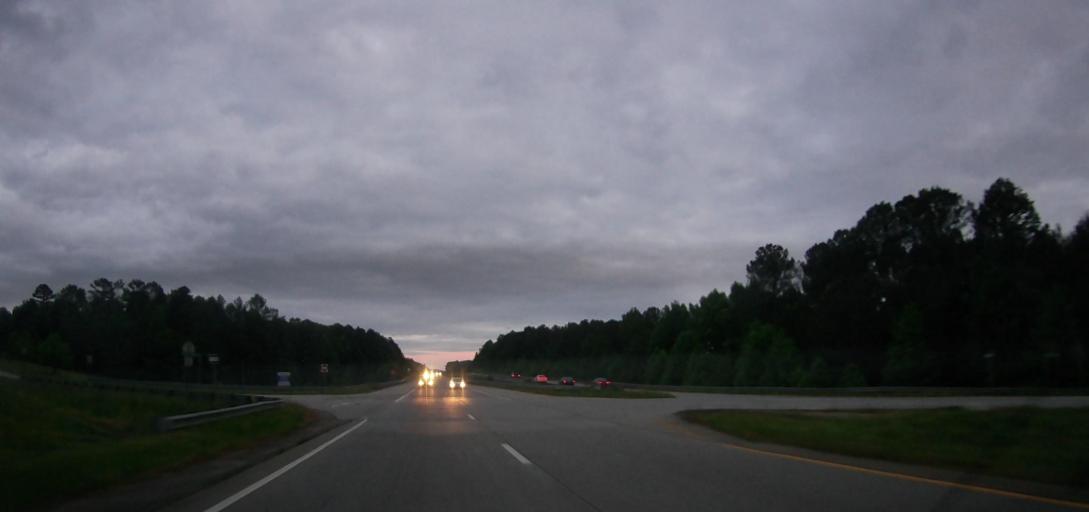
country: US
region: Georgia
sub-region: Jackson County
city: Jefferson
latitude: 34.1318
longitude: -83.6108
